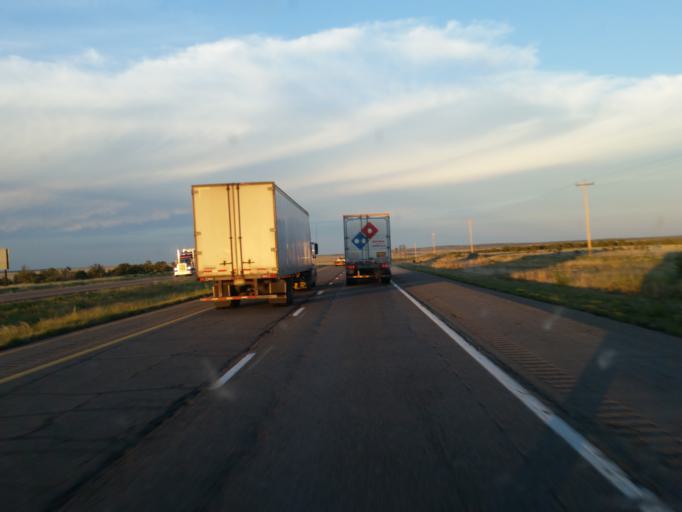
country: US
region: New Mexico
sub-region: San Miguel County
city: Las Vegas
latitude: 34.9930
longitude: -105.3279
